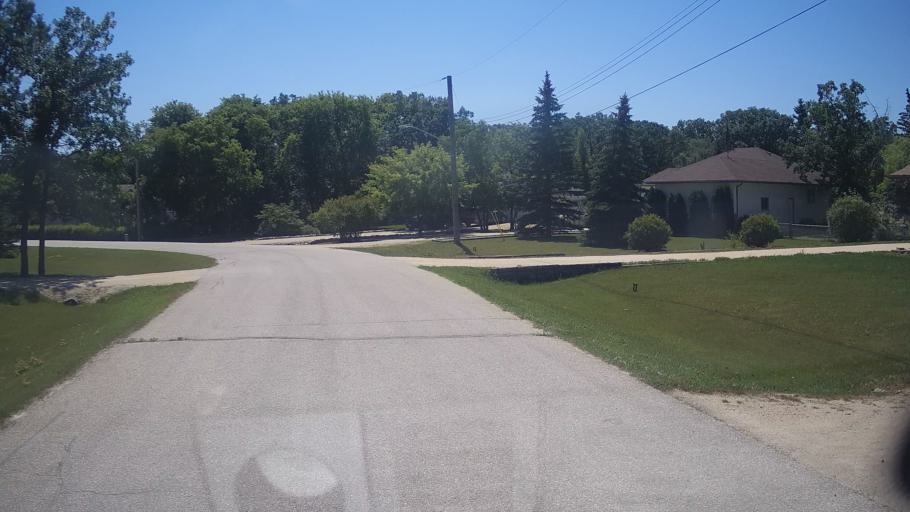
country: CA
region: Manitoba
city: Stonewall
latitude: 50.1331
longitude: -97.5496
